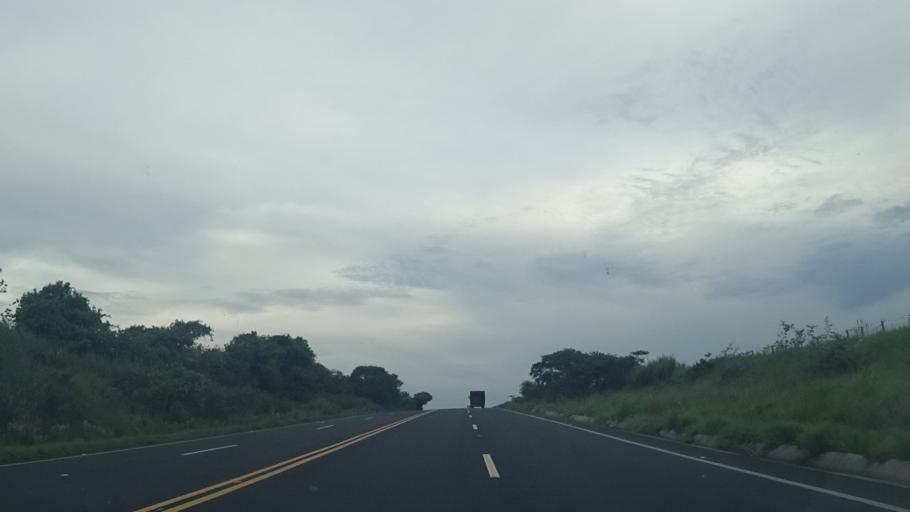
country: BR
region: Sao Paulo
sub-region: Martinopolis
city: Martinopolis
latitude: -22.0678
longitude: -51.1019
